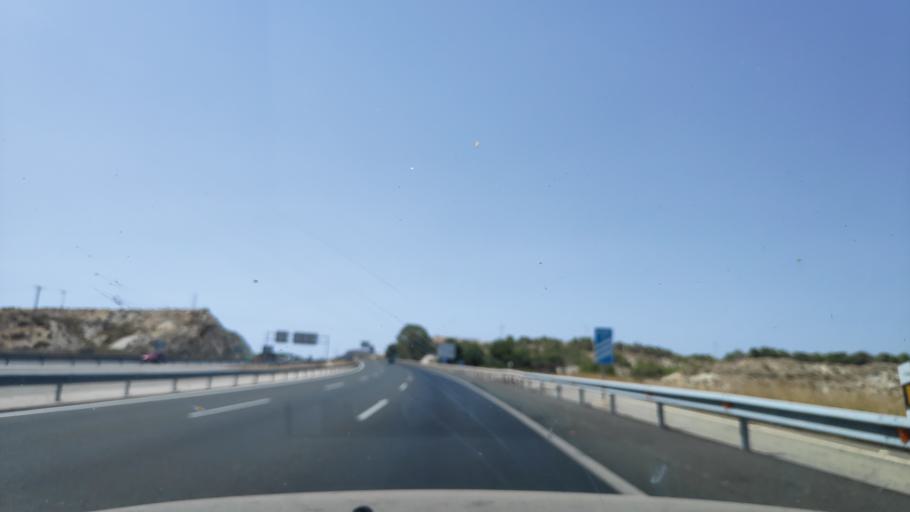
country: ES
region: Murcia
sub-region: Murcia
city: Murcia
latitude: 37.8790
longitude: -1.1308
